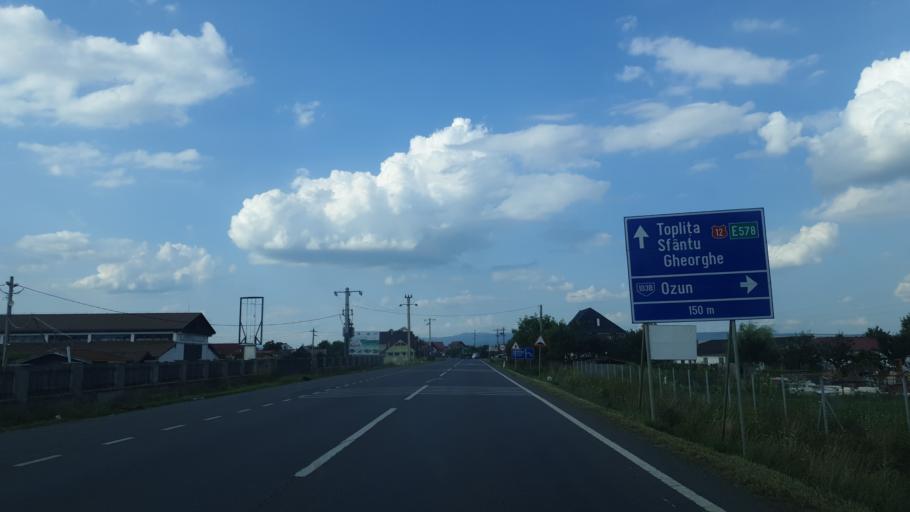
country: RO
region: Covasna
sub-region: Municipiul Sfantu Gheorghe
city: Sfantu-Gheorghe
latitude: 45.8305
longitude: 25.8034
